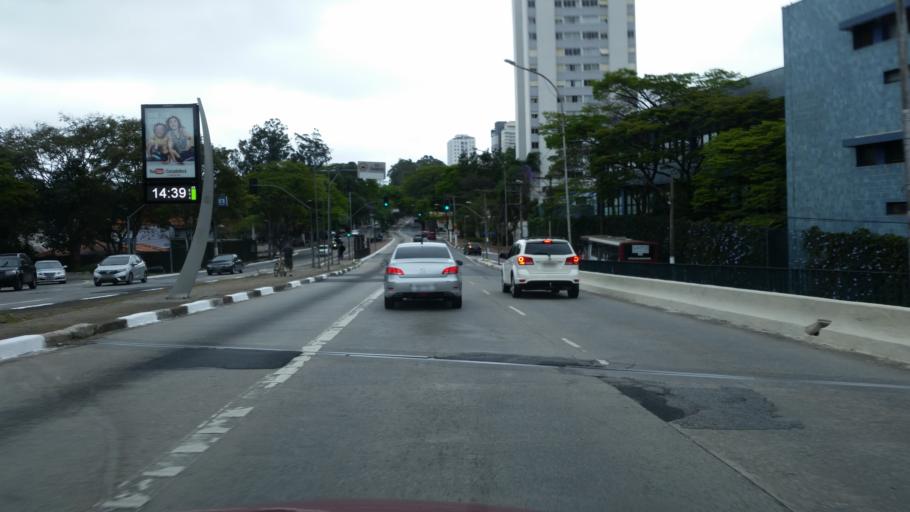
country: BR
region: Sao Paulo
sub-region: Diadema
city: Diadema
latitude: -23.6285
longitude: -46.6858
